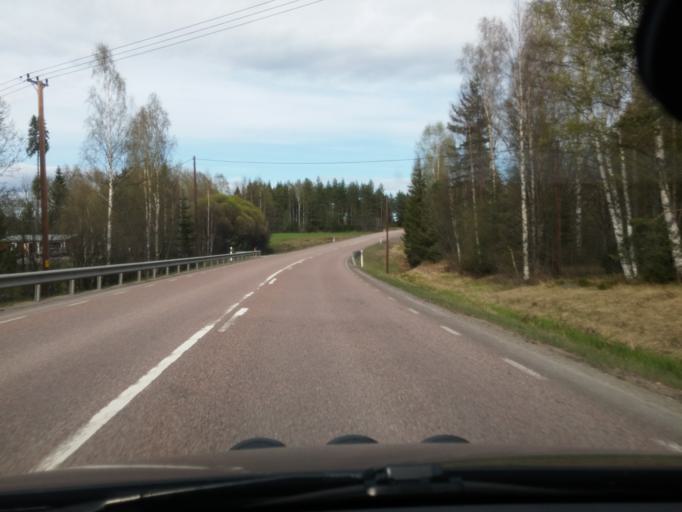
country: SE
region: Gaevleborg
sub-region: Ljusdals Kommun
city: Farila
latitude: 61.8123
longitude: 15.9585
